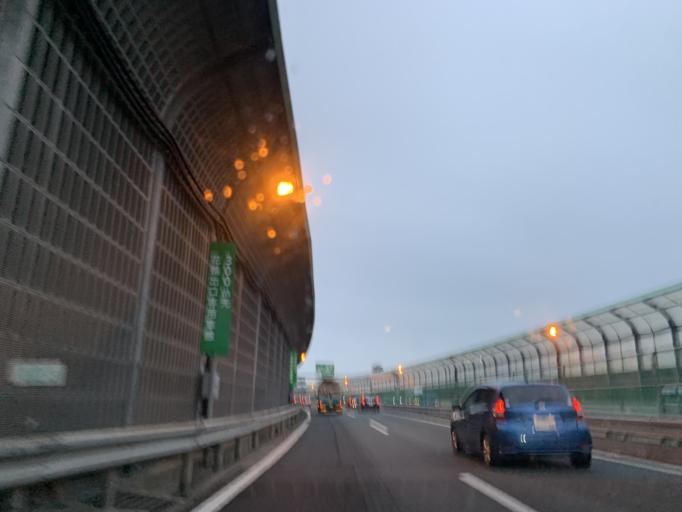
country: JP
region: Chiba
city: Funabashi
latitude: 35.6822
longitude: 140.0093
